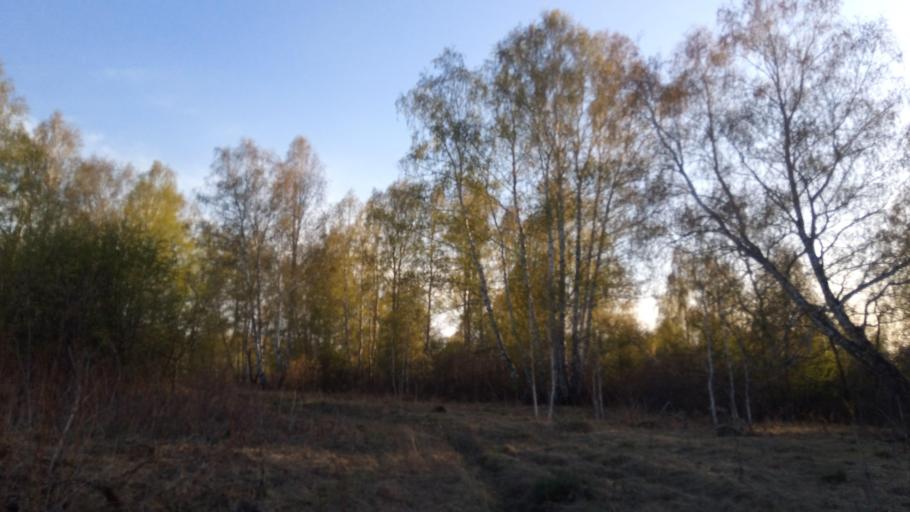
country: RU
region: Chelyabinsk
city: Timiryazevskiy
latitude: 54.9947
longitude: 60.8429
